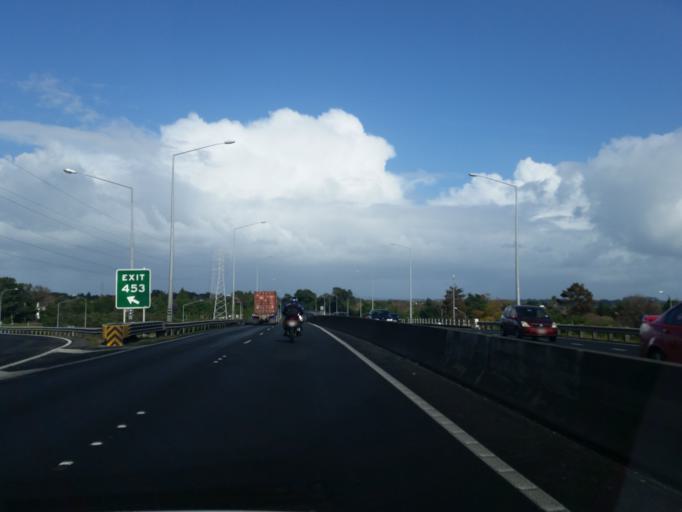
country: NZ
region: Auckland
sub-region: Auckland
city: Takanini
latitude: -37.0352
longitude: 174.9101
